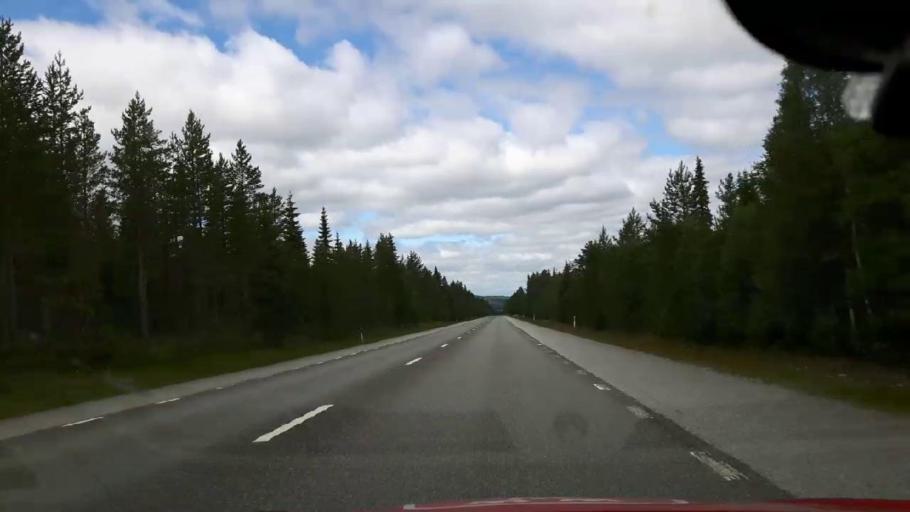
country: SE
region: Jaemtland
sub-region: Braecke Kommun
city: Braecke
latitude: 62.7076
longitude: 15.4896
